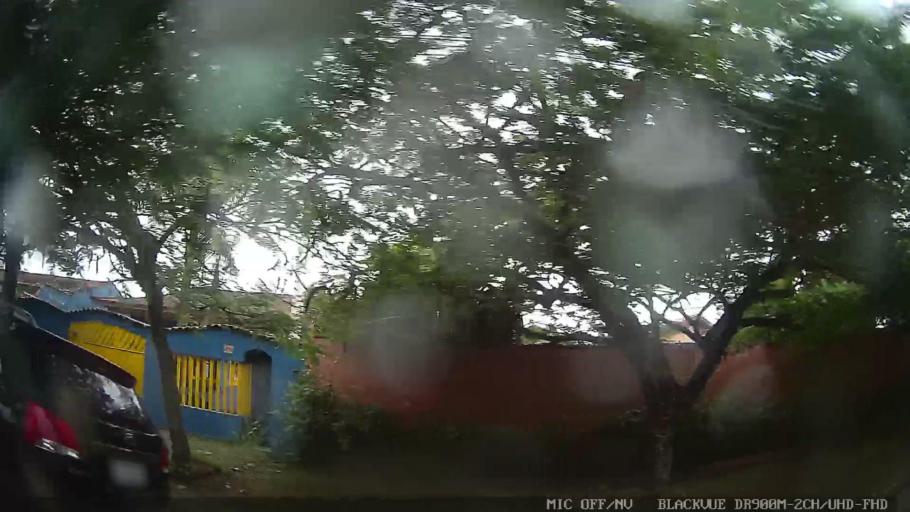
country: BR
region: Sao Paulo
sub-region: Mongagua
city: Mongagua
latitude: -24.1360
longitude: -46.7006
